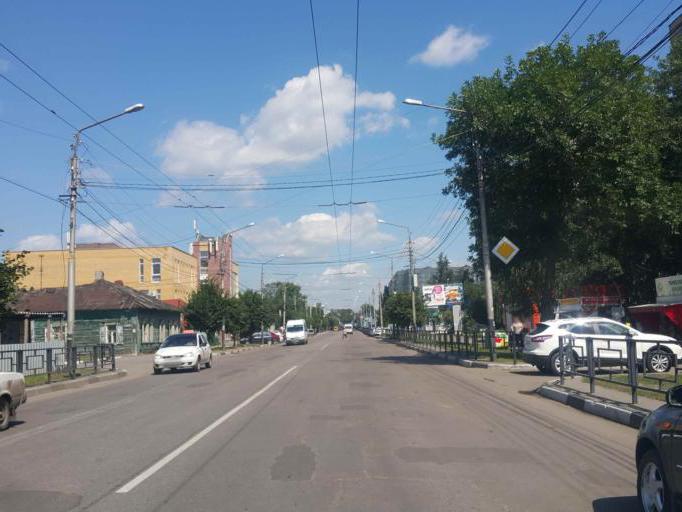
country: RU
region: Tambov
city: Tambov
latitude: 52.7291
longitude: 41.4429
